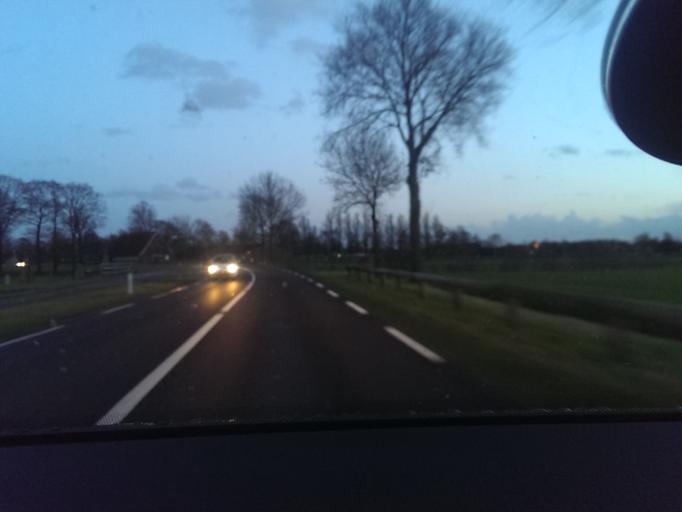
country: NL
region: Overijssel
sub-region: Gemeente Twenterand
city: Magele
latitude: 52.4449
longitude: 6.5258
